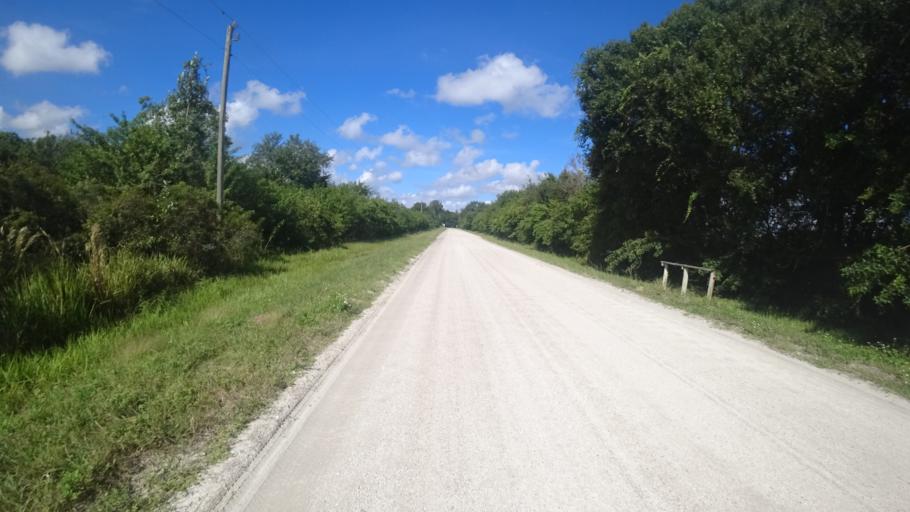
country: US
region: Florida
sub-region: Sarasota County
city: Lake Sarasota
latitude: 27.3668
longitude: -82.1389
